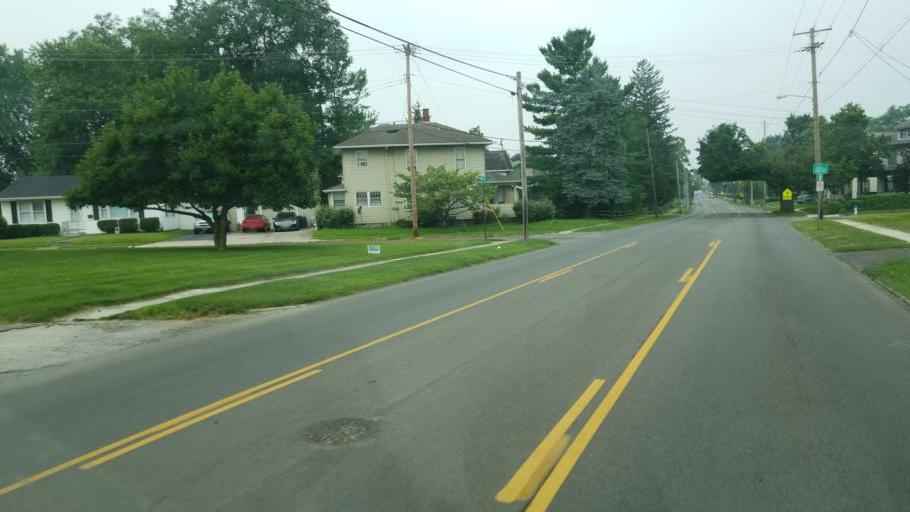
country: US
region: Ohio
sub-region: Marion County
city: Marion
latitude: 40.5838
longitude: -83.1157
